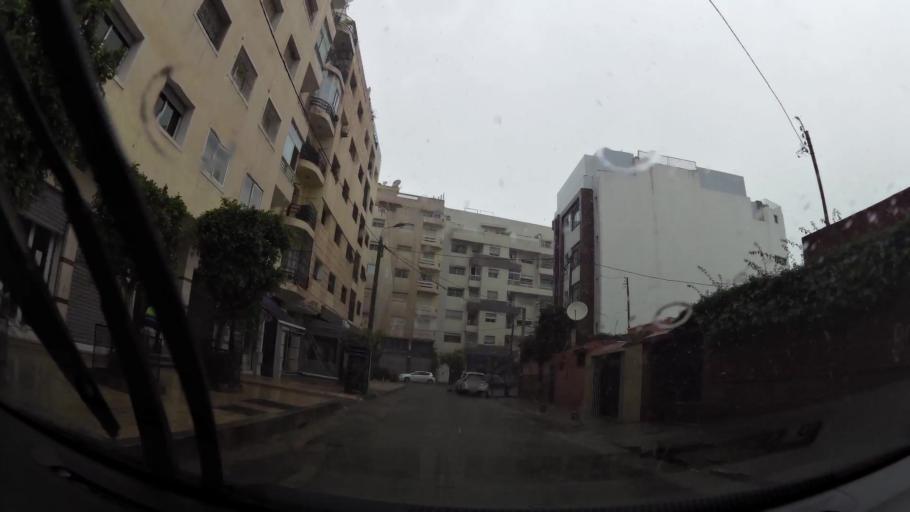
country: MA
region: Grand Casablanca
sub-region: Casablanca
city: Casablanca
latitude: 33.5736
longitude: -7.6310
